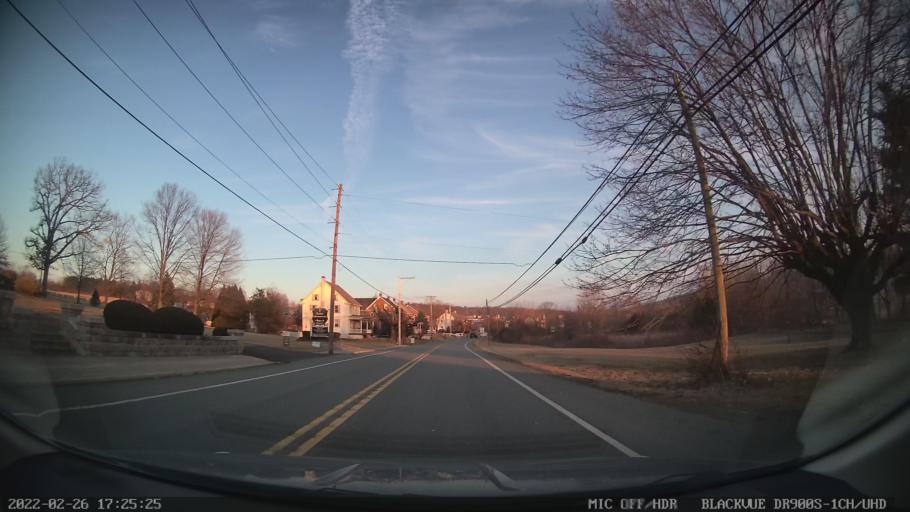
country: US
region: Pennsylvania
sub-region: Montgomery County
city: East Greenville
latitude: 40.4284
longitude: -75.5369
